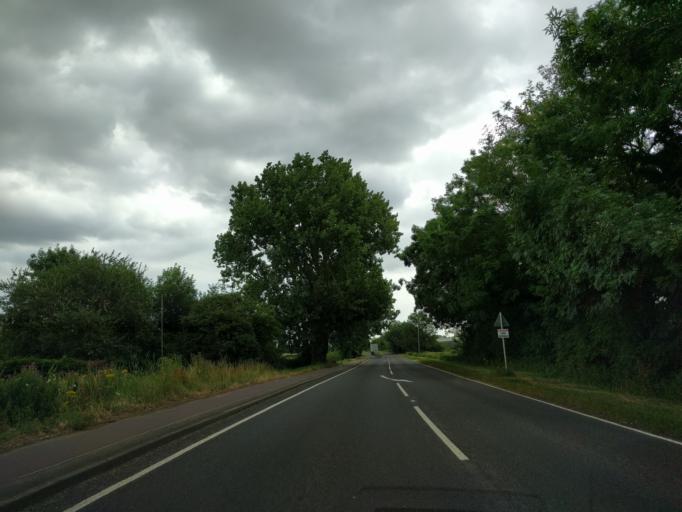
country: GB
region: England
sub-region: Cambridgeshire
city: Needingworth
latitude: 52.3315
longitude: -0.0572
